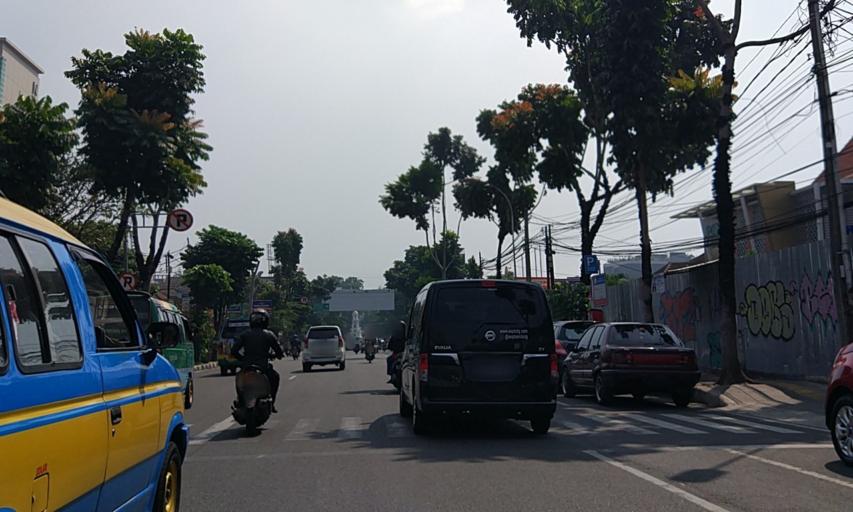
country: ID
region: West Java
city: Bandung
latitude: -6.9066
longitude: 107.6045
